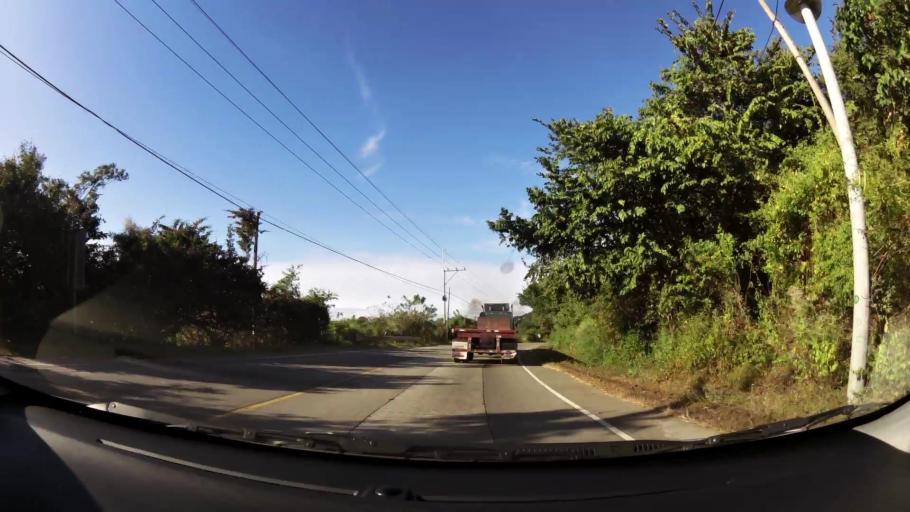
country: SV
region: Santa Ana
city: Metapan
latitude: 14.2567
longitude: -89.4610
